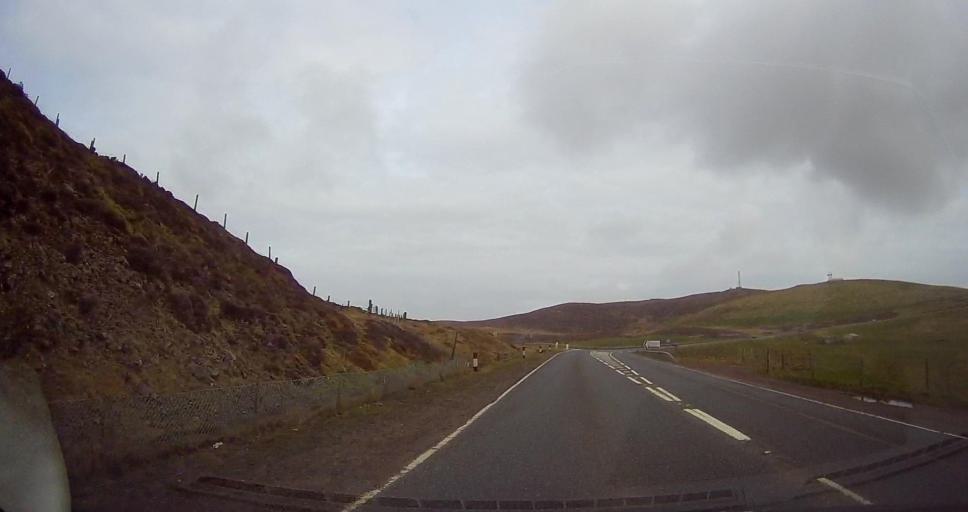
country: GB
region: Scotland
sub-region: Shetland Islands
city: Lerwick
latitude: 60.1353
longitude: -1.2138
